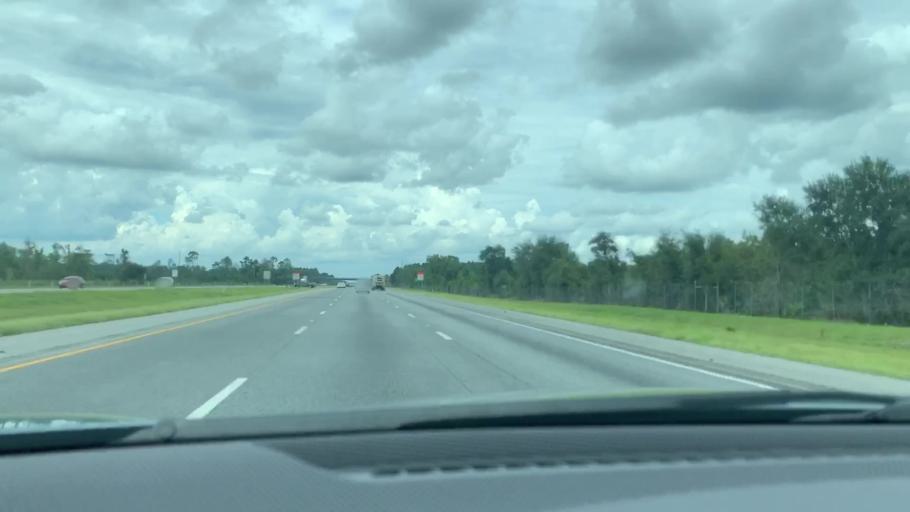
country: US
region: Georgia
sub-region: McIntosh County
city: Darien
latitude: 31.4253
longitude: -81.4433
